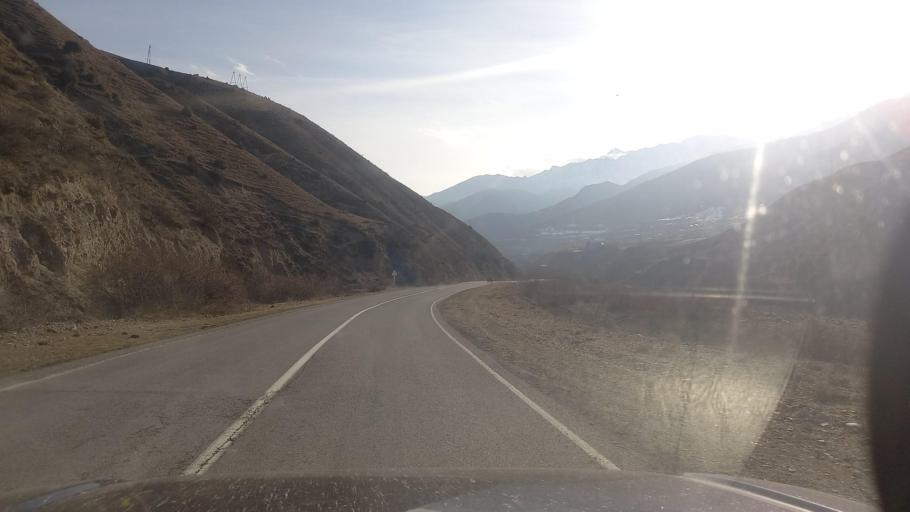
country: RU
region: Ingushetiya
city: Dzhayrakh
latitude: 42.8404
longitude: 44.6571
